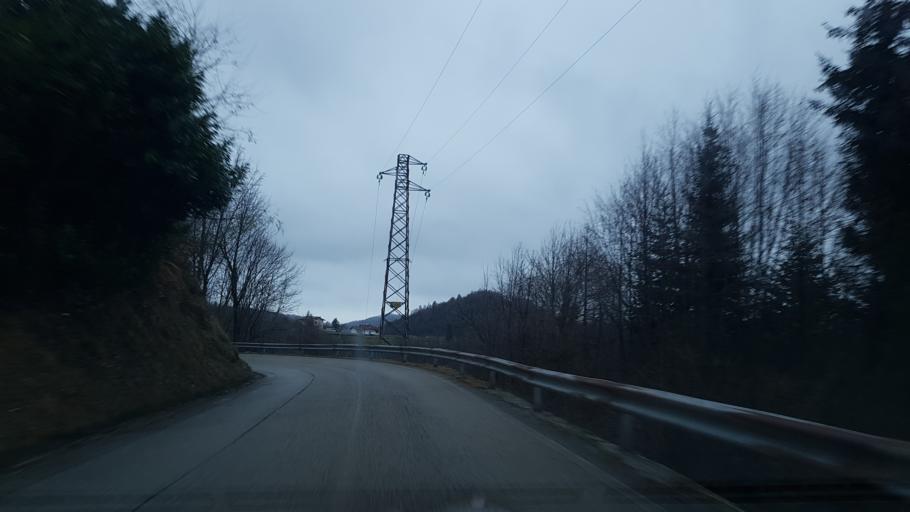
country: IT
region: Friuli Venezia Giulia
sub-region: Provincia di Udine
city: Clodig
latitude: 46.1385
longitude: 13.6150
